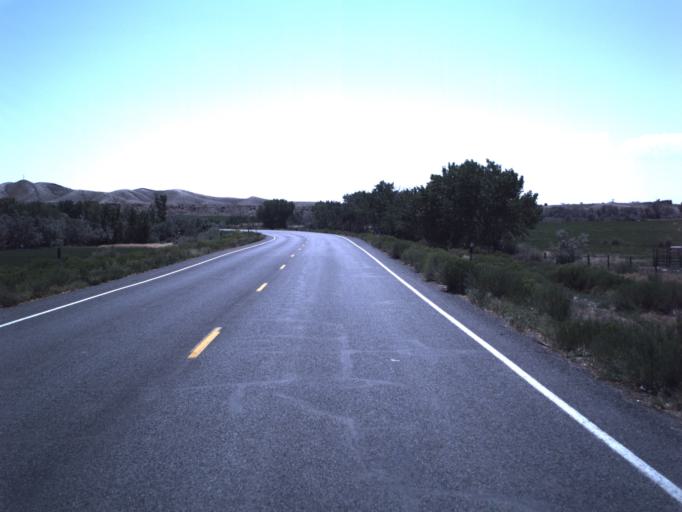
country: US
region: Utah
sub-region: Emery County
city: Orangeville
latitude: 39.2200
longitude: -111.0685
